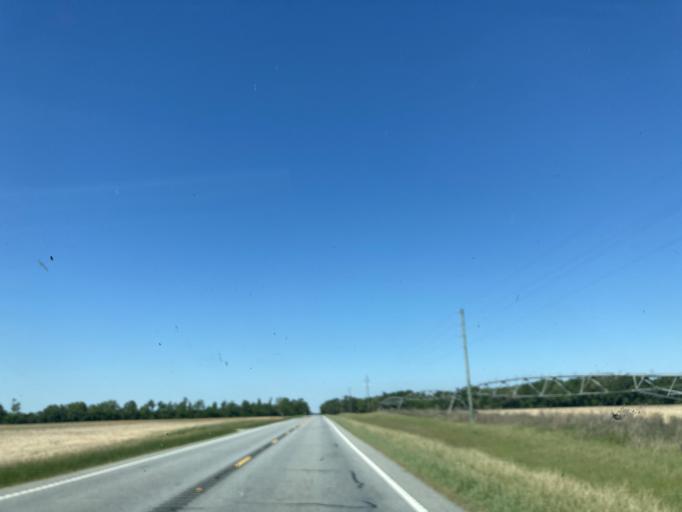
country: US
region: Georgia
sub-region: Baker County
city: Newton
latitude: 31.2227
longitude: -84.4471
